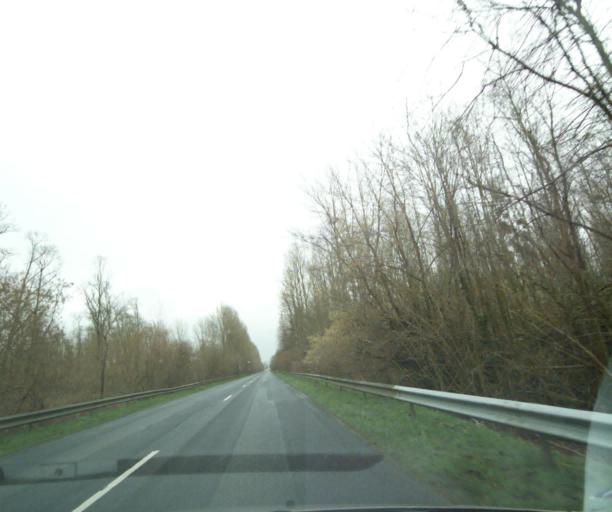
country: FR
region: Picardie
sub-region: Departement de l'Oise
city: Noyon
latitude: 49.5608
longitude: 3.0351
